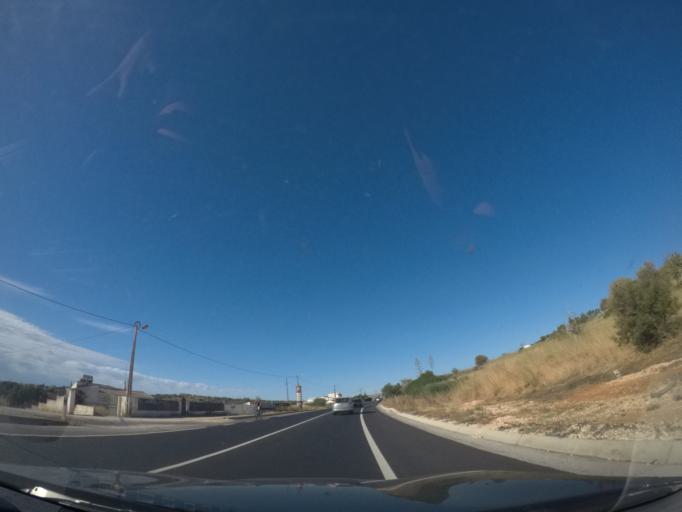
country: PT
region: Faro
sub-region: Lagos
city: Lagos
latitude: 37.1344
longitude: -8.6642
